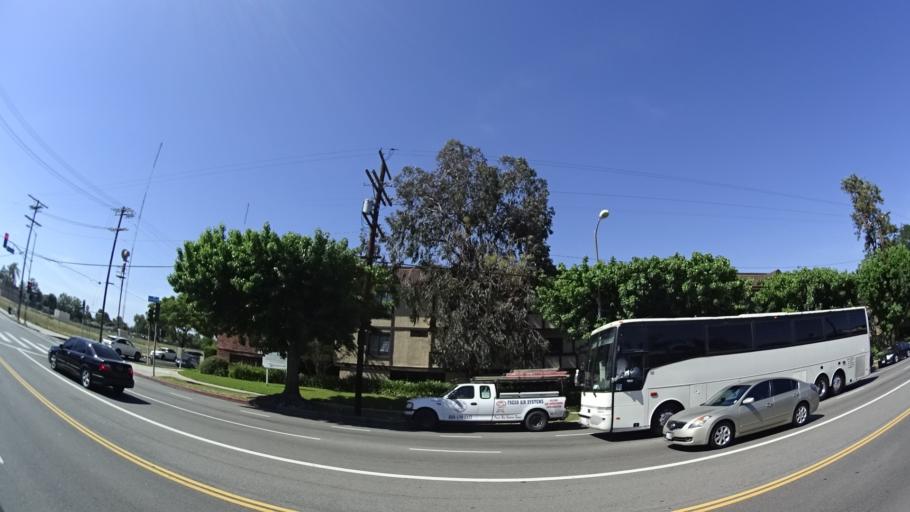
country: US
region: California
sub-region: Los Angeles County
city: North Hollywood
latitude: 34.1721
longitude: -118.4091
